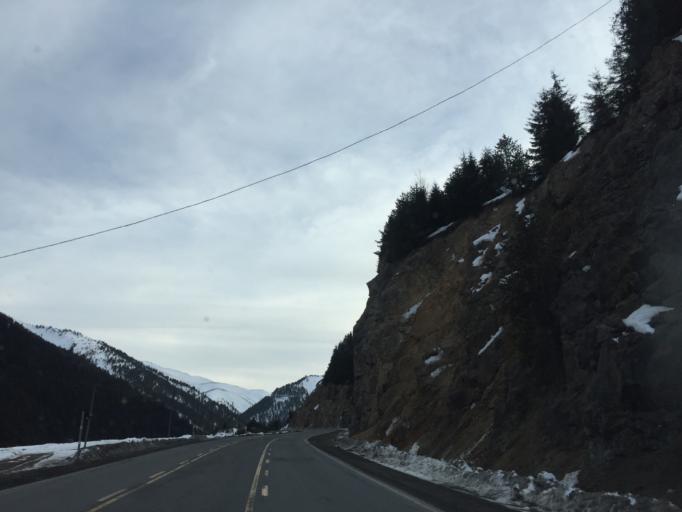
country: TR
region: Gumushane
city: Yaglidere
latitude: 40.6723
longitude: 39.4182
